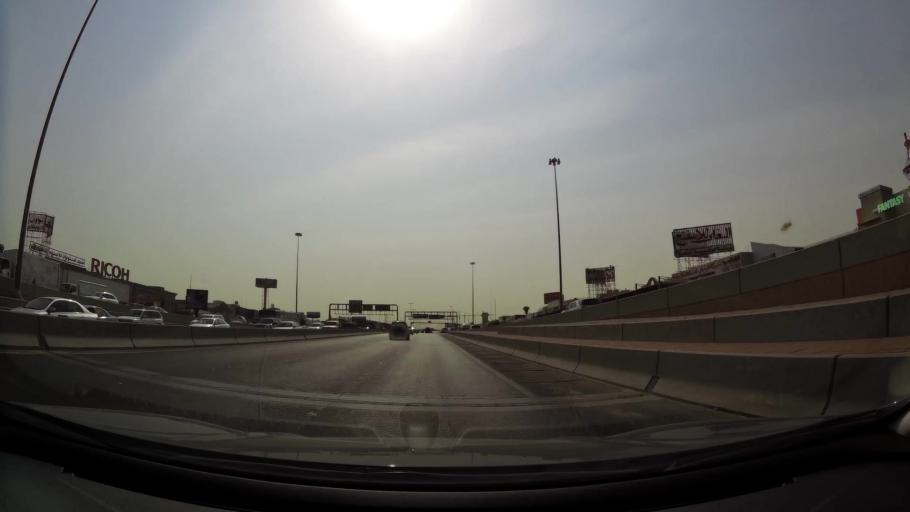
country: KW
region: Al Asimah
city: Ar Rabiyah
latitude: 29.3130
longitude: 47.9425
